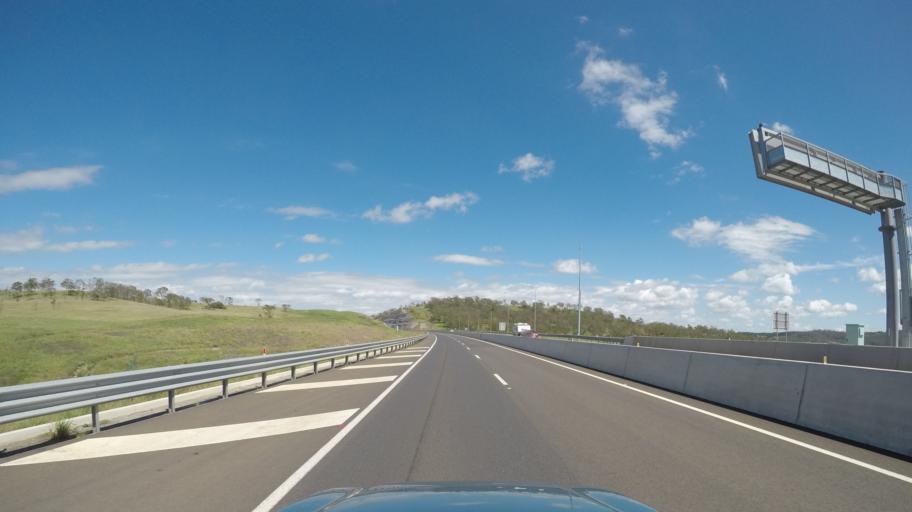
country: AU
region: Queensland
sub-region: Toowoomba
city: Wilsonton Heights
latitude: -27.5099
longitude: 151.9222
